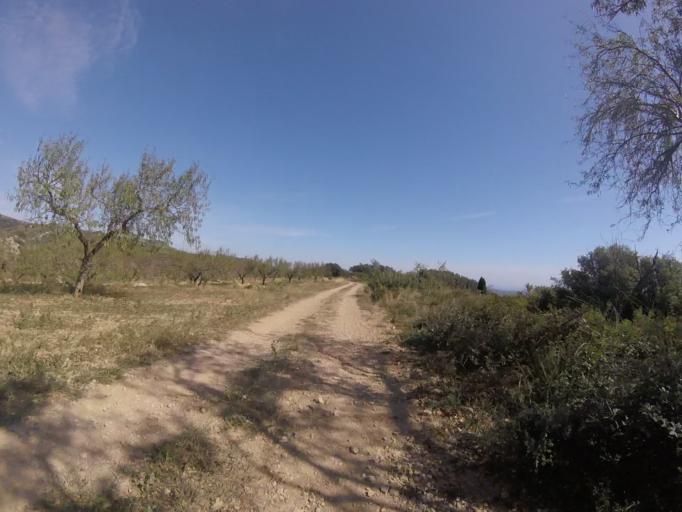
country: ES
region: Valencia
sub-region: Provincia de Castello
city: Sierra-Engarceran
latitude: 40.2717
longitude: 0.0068
